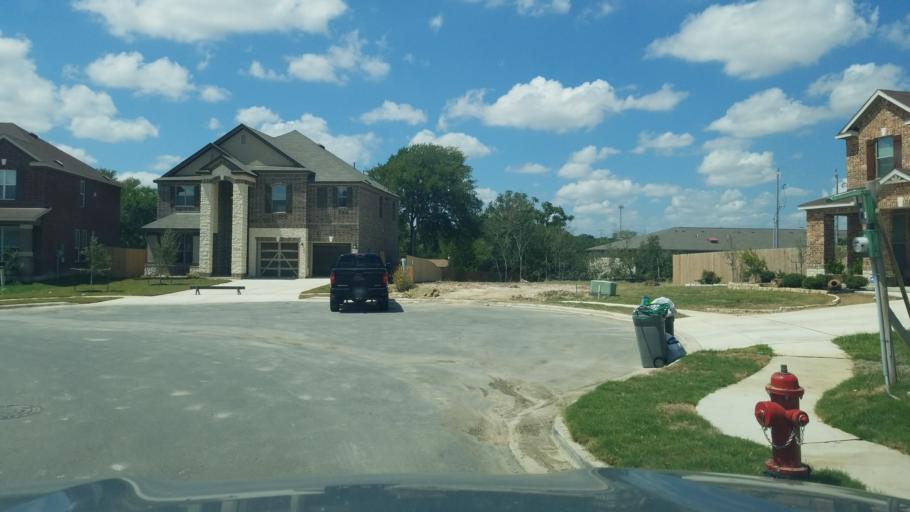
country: US
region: Texas
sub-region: Bexar County
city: Converse
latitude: 29.5384
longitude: -98.3253
